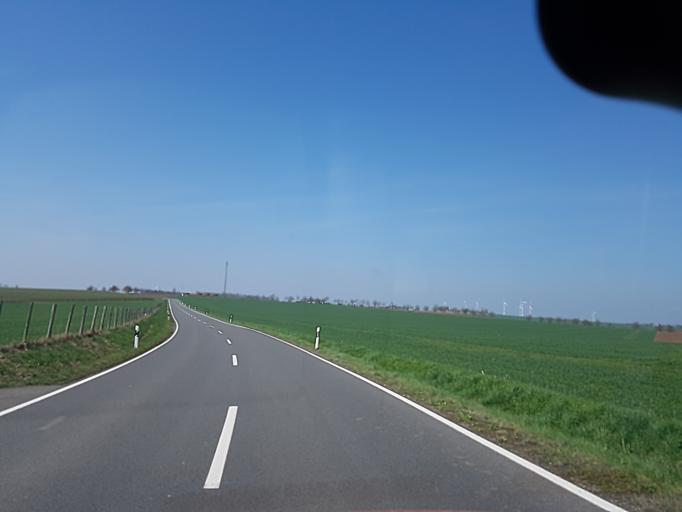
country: DE
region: Saxony
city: Ostrau
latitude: 51.2170
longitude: 12.8733
